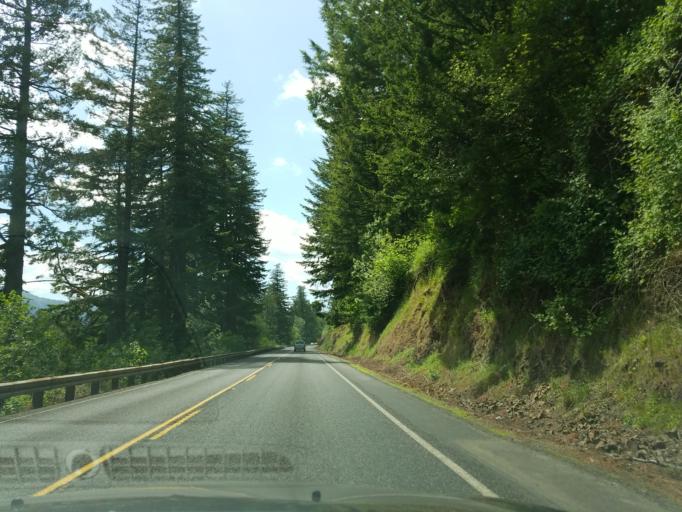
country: US
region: Oregon
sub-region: Hood River County
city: Cascade Locks
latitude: 45.6093
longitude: -122.0675
